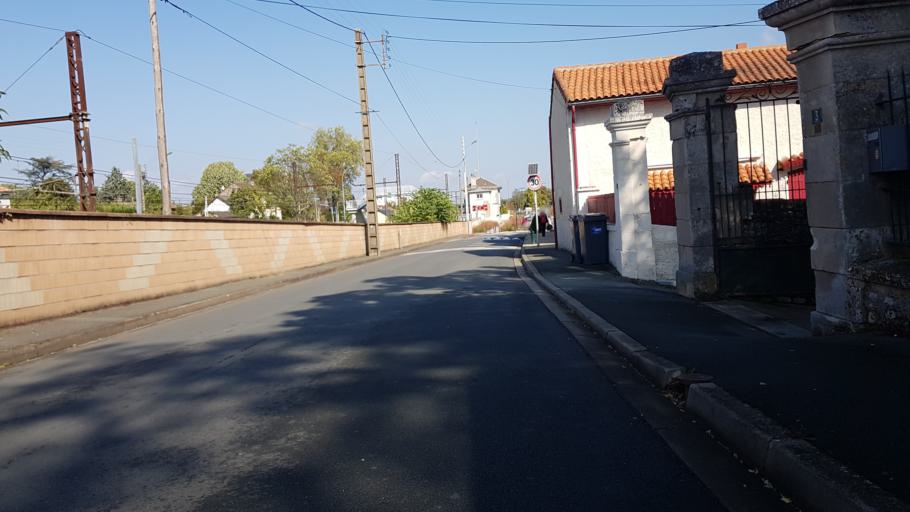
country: FR
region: Poitou-Charentes
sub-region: Departement de la Vienne
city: Chasseneuil-du-Poitou
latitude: 46.6506
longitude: 0.3723
